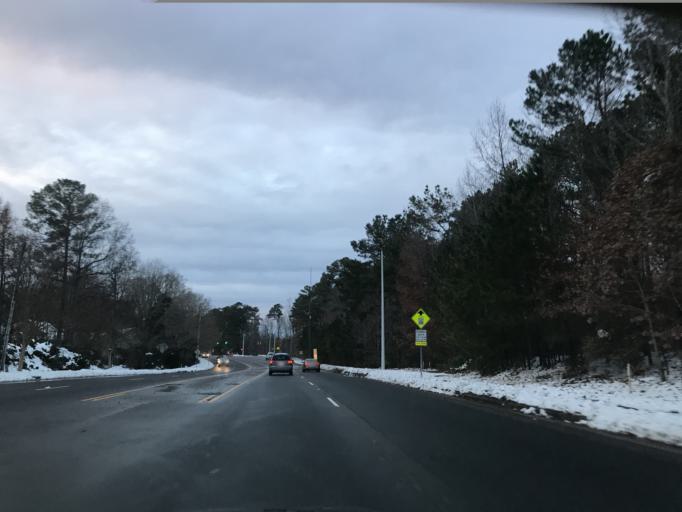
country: US
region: North Carolina
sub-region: Wake County
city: Wake Forest
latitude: 35.8991
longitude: -78.5752
